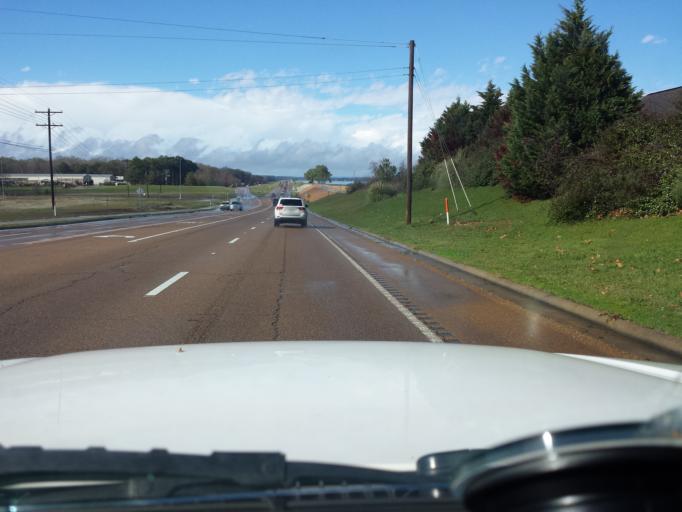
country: US
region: Mississippi
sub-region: Madison County
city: Ridgeland
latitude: 32.3847
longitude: -90.0446
